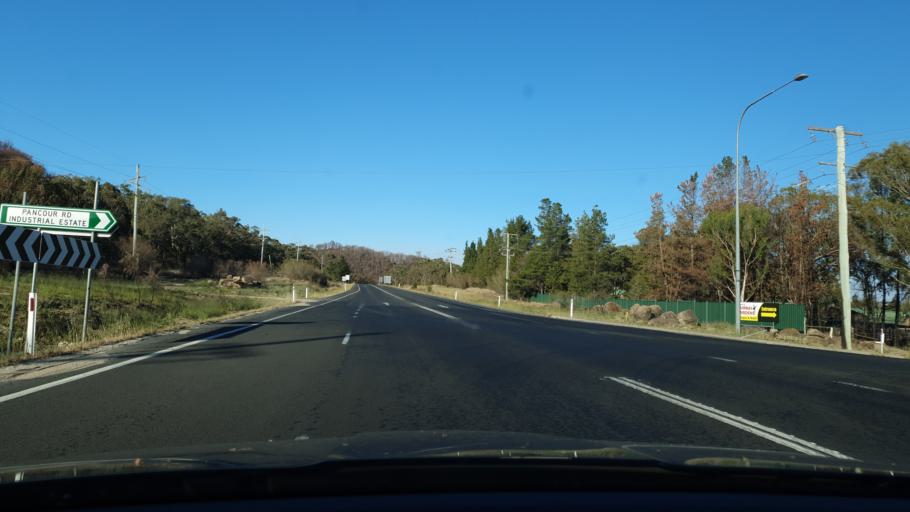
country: AU
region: Queensland
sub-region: Southern Downs
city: Stanthorpe
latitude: -28.6491
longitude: 151.9232
